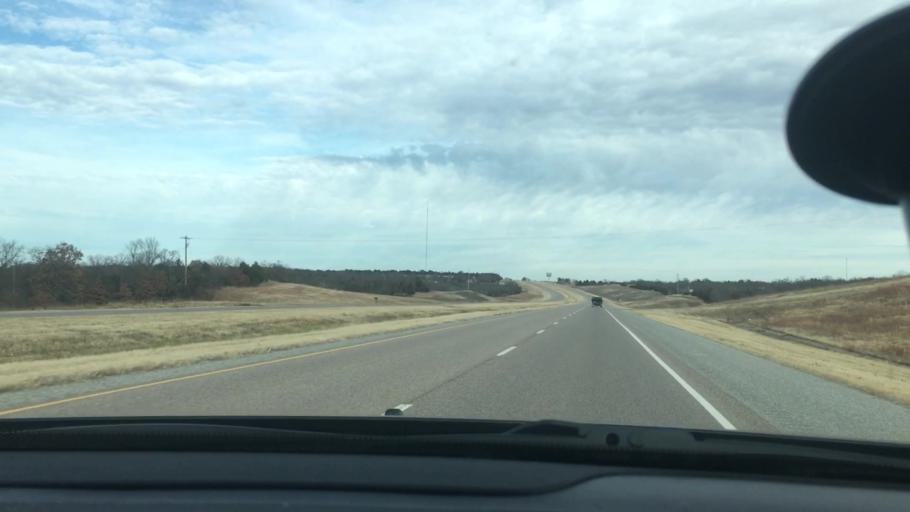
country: US
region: Oklahoma
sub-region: Pontotoc County
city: Byng
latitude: 34.8779
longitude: -96.6768
